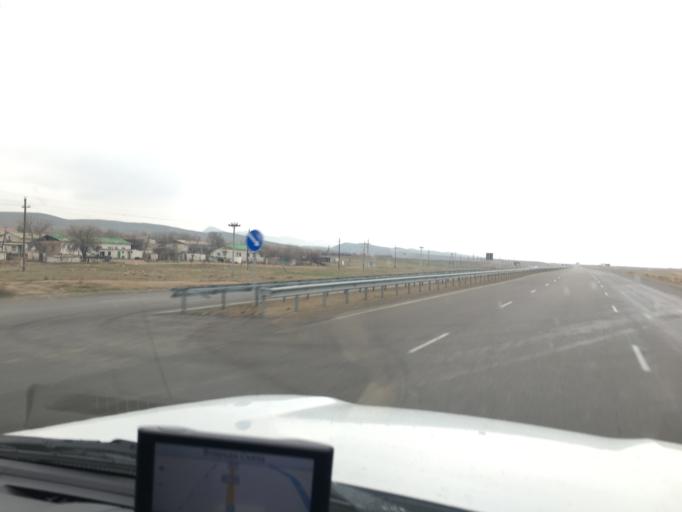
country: IR
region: Razavi Khorasan
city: Dargaz
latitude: 37.6407
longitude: 59.1444
